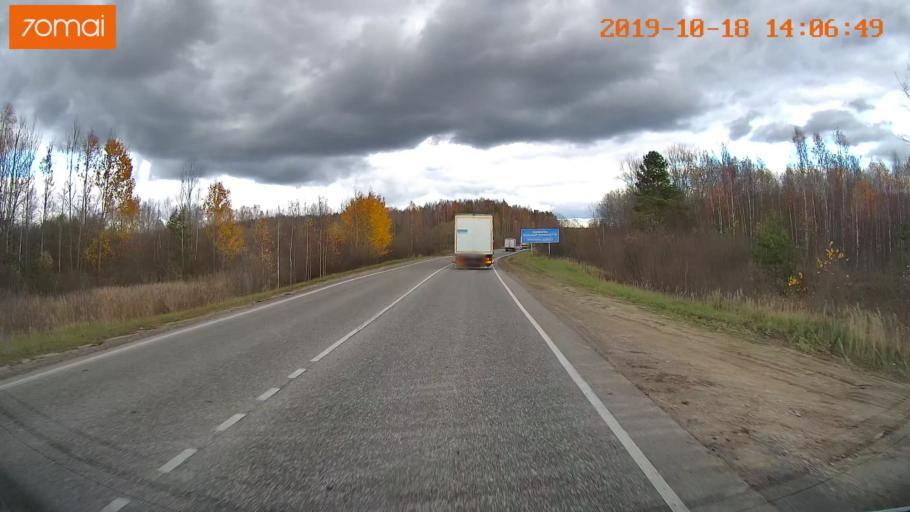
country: RU
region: Rjazan
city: Spas-Klepiki
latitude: 55.1491
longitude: 40.1539
